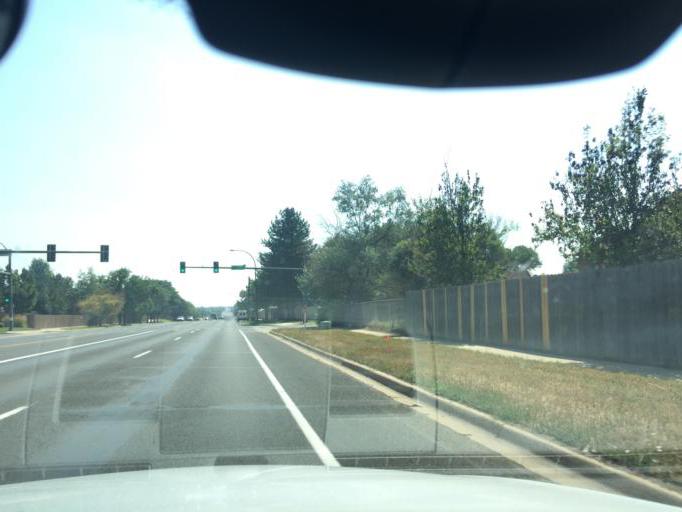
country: US
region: Colorado
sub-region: Broomfield County
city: Broomfield
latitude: 39.8997
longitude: -105.0593
